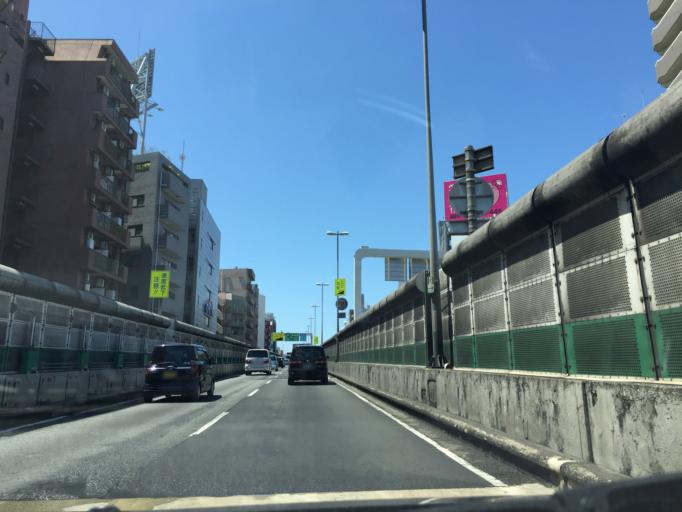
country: JP
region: Tokyo
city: Tokyo
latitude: 35.6481
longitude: 139.6798
